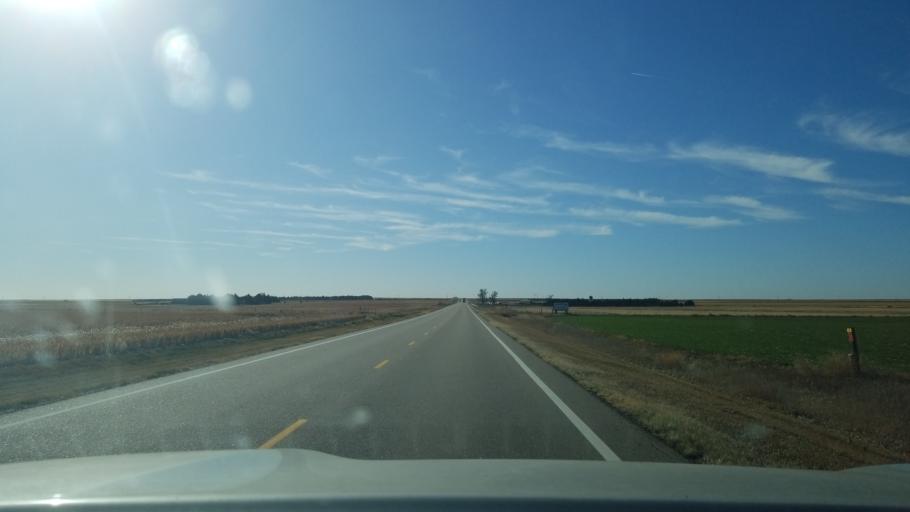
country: US
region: Kansas
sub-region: Ness County
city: Ness City
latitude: 38.3722
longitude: -99.8979
